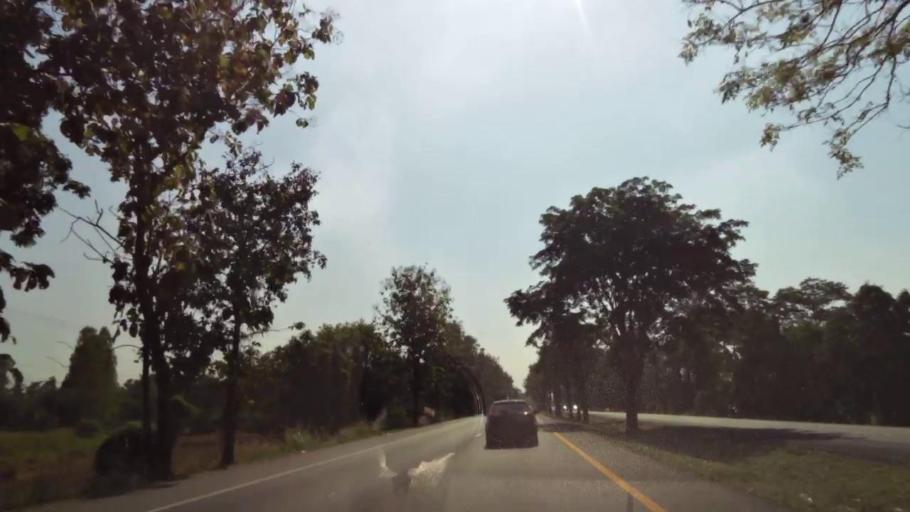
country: TH
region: Phichit
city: Bueng Na Rang
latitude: 16.0601
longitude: 100.1228
